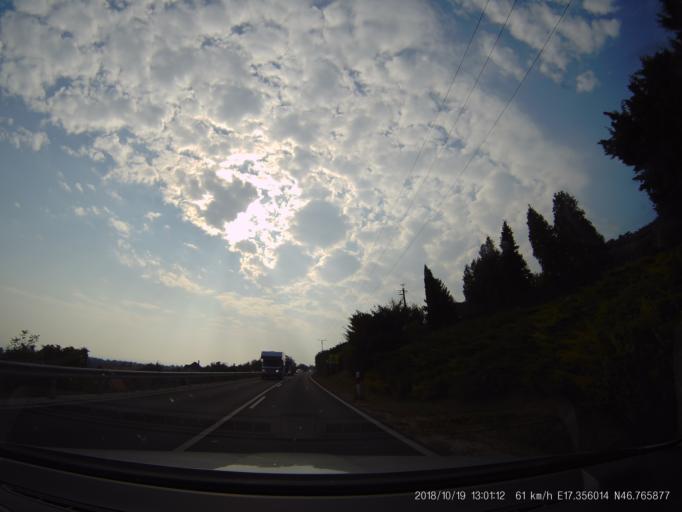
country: HU
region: Zala
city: Vonyarcvashegy
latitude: 46.7658
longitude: 17.3559
